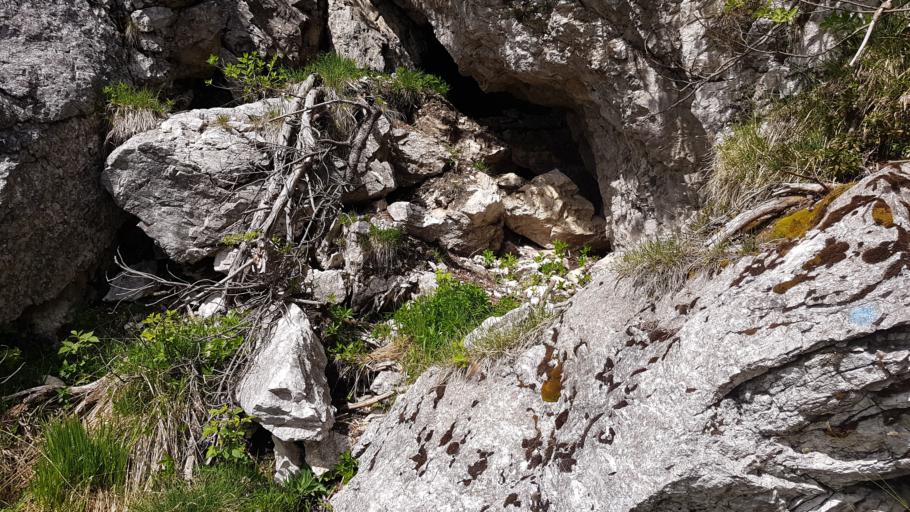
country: IT
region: Friuli Venezia Giulia
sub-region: Provincia di Udine
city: Moggio Udinese
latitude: 46.4783
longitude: 13.2087
